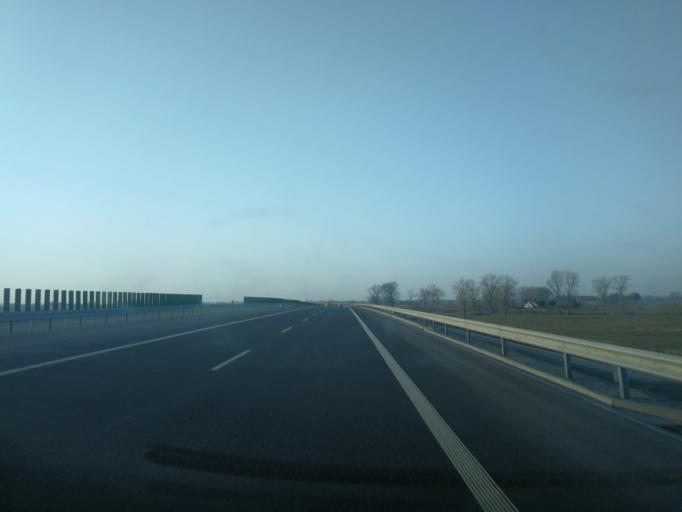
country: PL
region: Pomeranian Voivodeship
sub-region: Powiat nowodworski
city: Nowy Dwor Gdanski
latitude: 54.1808
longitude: 19.1812
